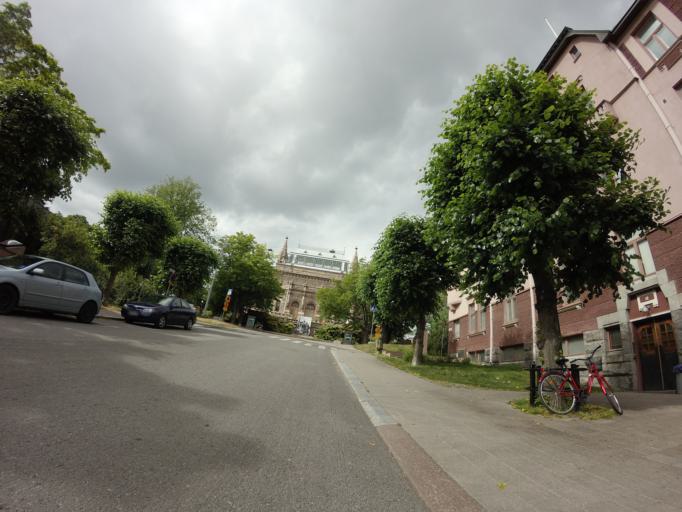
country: FI
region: Varsinais-Suomi
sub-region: Turku
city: Turku
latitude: 60.4534
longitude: 22.2627
